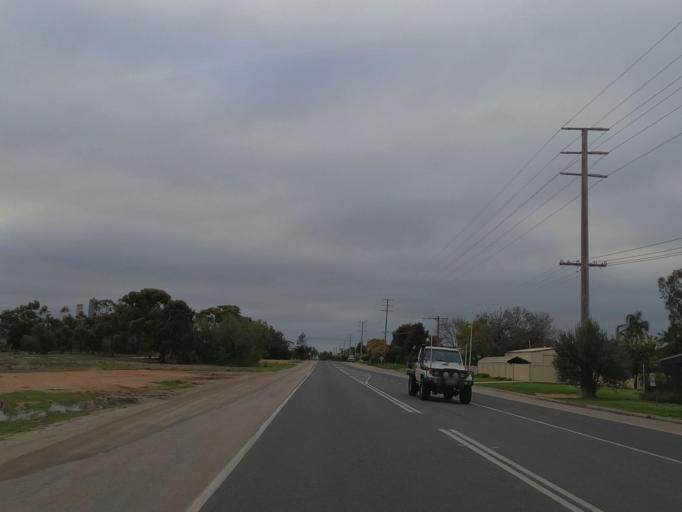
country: AU
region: Victoria
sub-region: Swan Hill
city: Swan Hill
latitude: -35.4615
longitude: 143.6341
